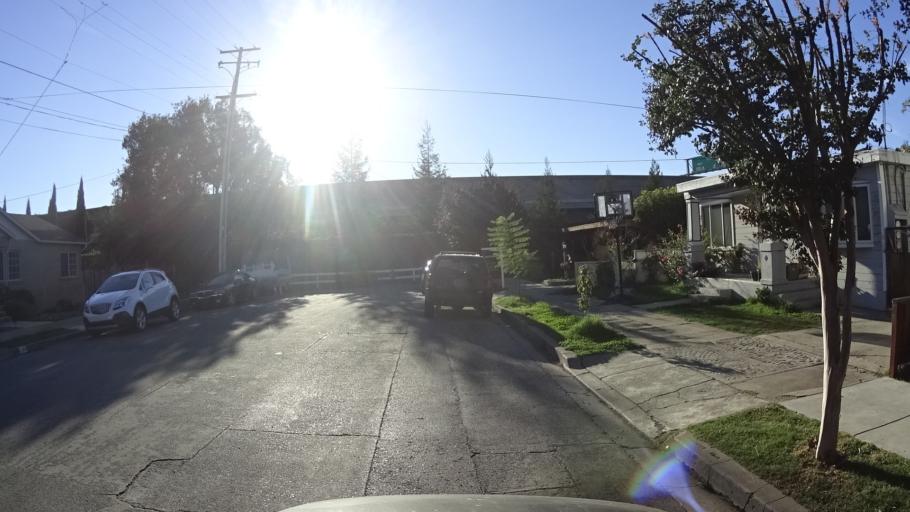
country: US
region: California
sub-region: Santa Clara County
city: San Jose
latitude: 37.3463
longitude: -121.9025
